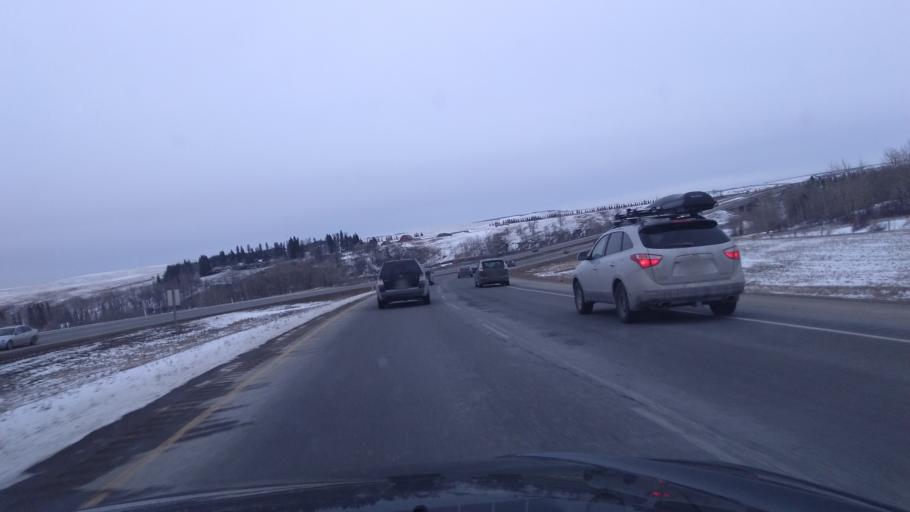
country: CA
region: Alberta
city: Cochrane
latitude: 51.0930
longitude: -114.5522
